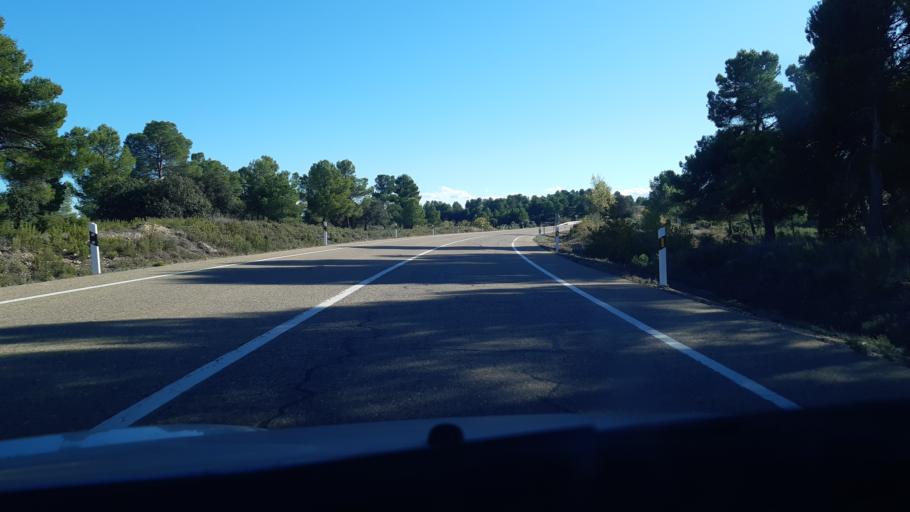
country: ES
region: Aragon
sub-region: Provincia de Teruel
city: Valjunquera
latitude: 40.9396
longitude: -0.0115
